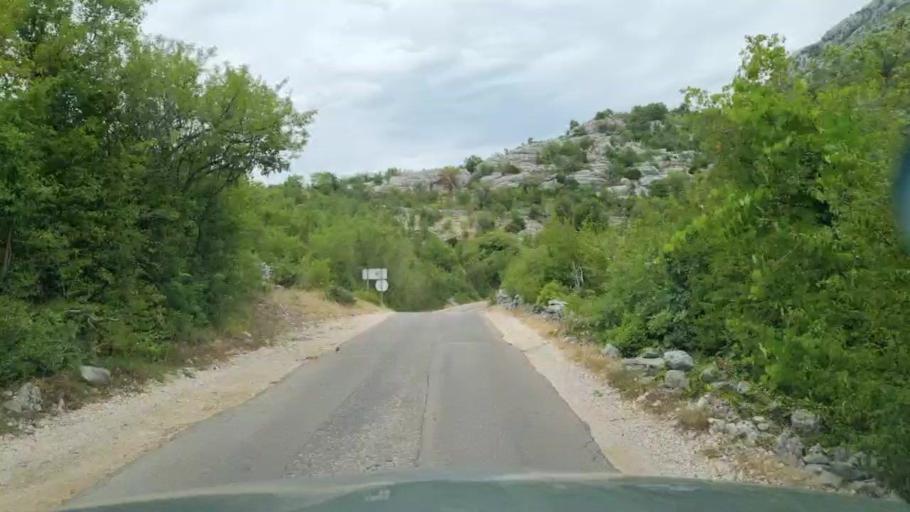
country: HR
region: Dubrovacko-Neretvanska
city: Podgora
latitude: 42.9654
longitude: 17.7955
